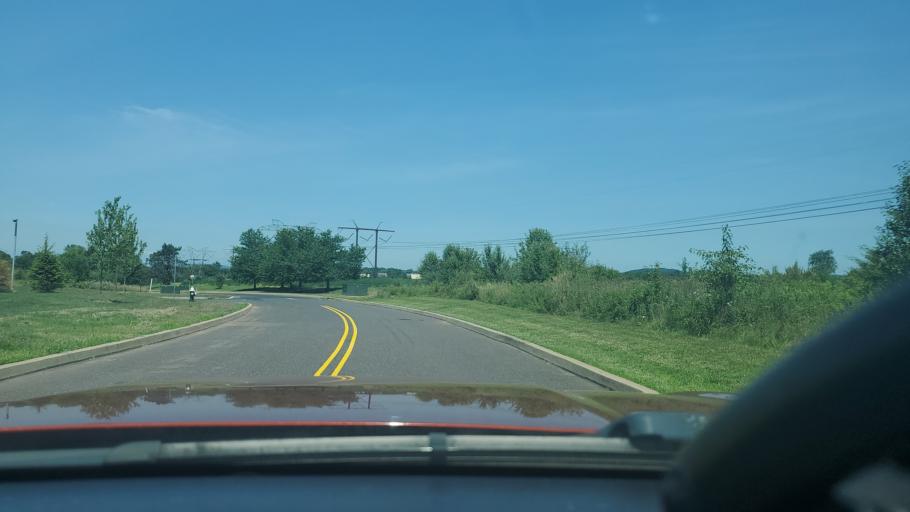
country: US
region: Pennsylvania
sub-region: Montgomery County
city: Limerick
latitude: 40.2236
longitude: -75.5510
